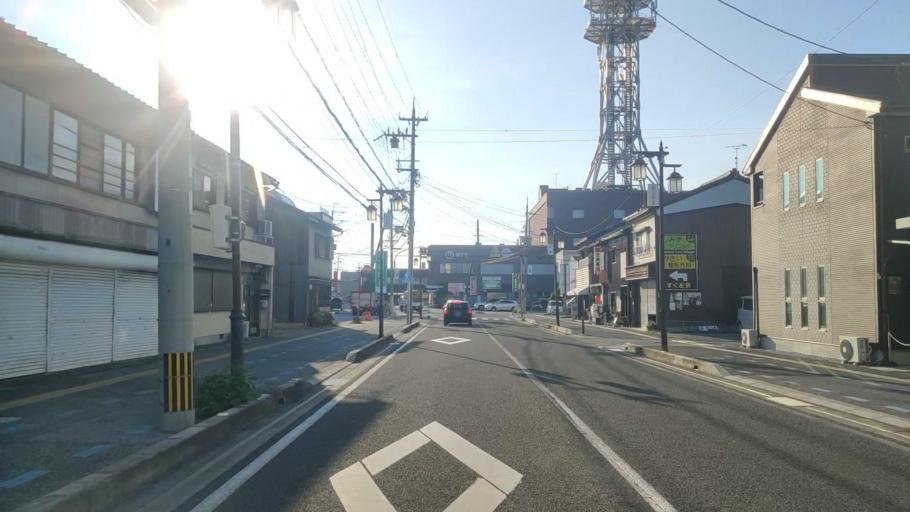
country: JP
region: Shiga Prefecture
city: Hikone
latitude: 35.2701
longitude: 136.2578
